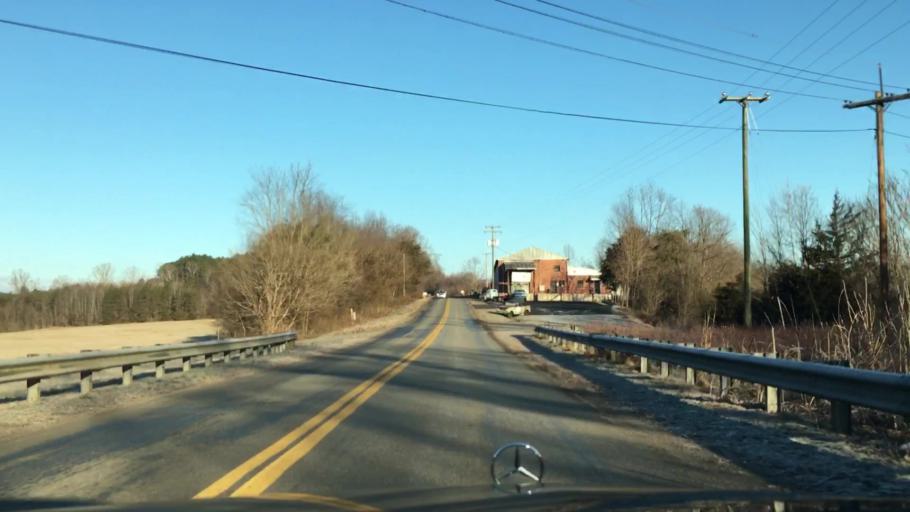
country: US
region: Virginia
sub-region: Pittsylvania County
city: Hurt
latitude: 37.1063
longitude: -79.3059
